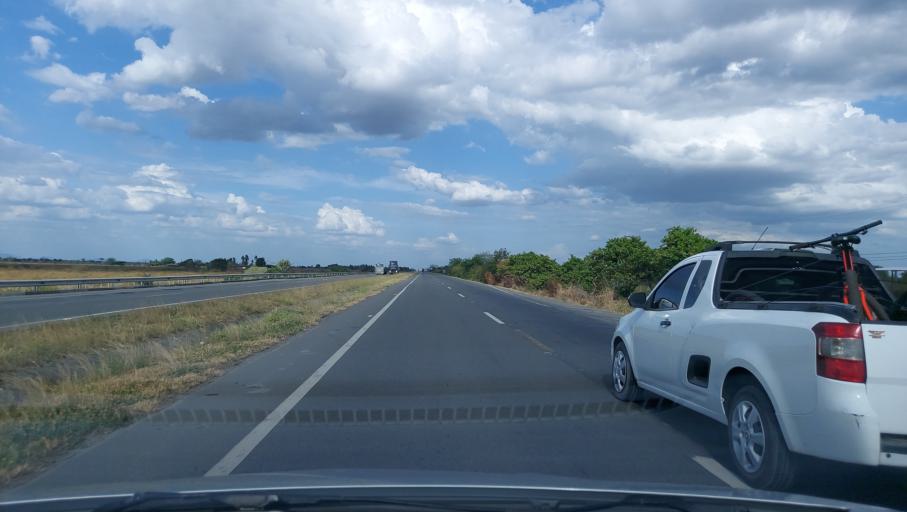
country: BR
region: Bahia
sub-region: Castro Alves
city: Castro Alves
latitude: -12.5580
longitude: -39.4678
